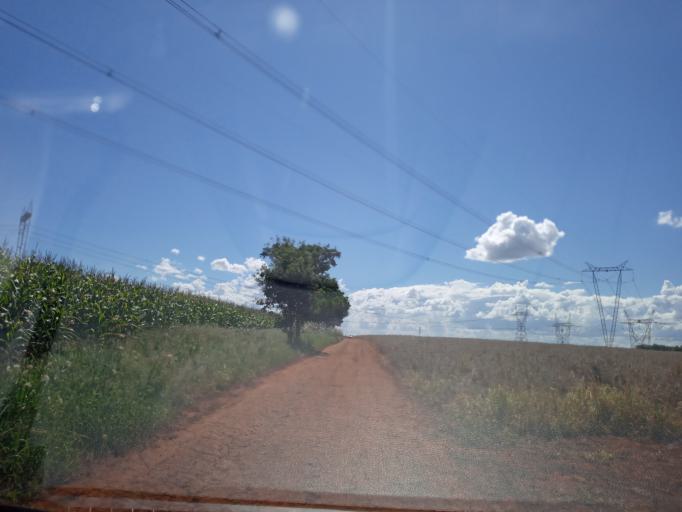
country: BR
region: Goias
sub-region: Itumbiara
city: Itumbiara
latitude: -18.4355
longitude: -49.1192
